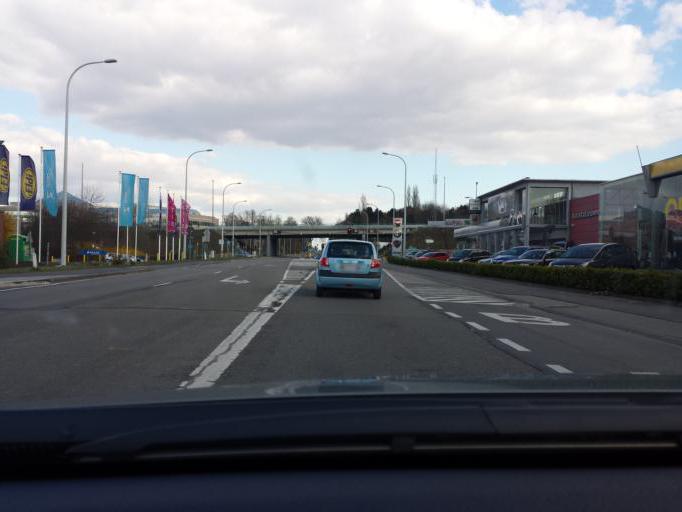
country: BE
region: Flanders
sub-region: Provincie Vlaams-Brabant
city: Herent
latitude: 50.8859
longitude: 4.6709
